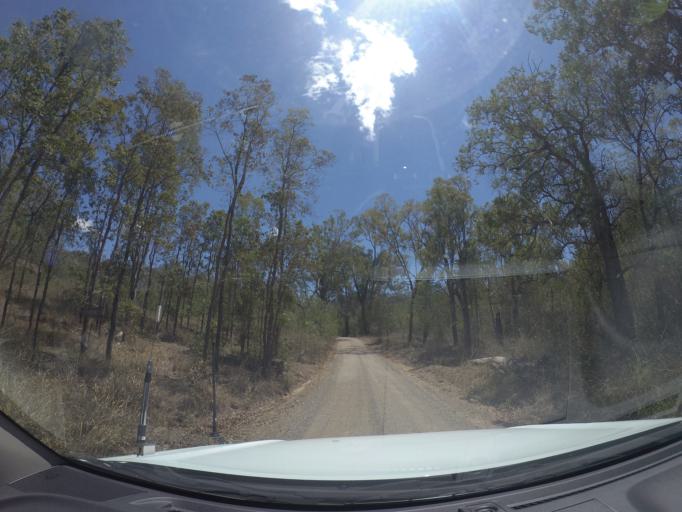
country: AU
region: Queensland
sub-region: Ipswich
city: Springfield Lakes
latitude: -27.8076
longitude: 152.8452
